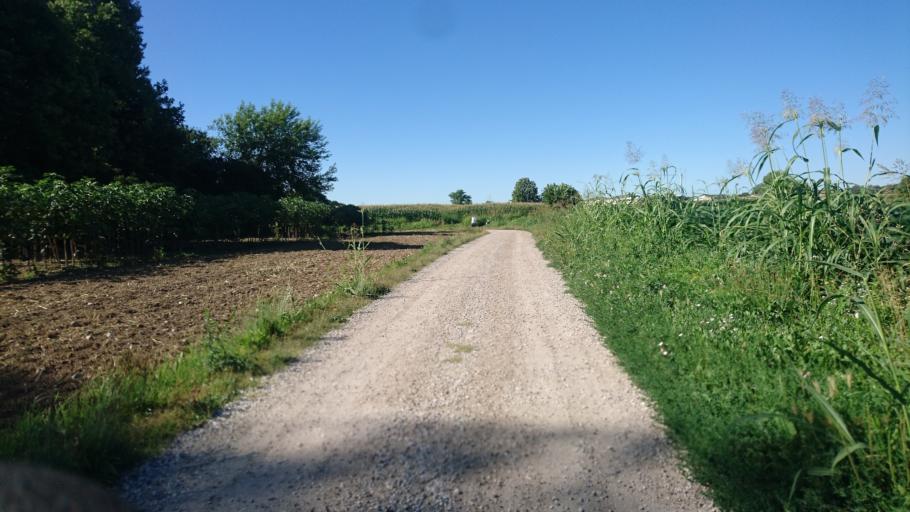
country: IT
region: Veneto
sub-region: Provincia di Padova
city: Legnaro
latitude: 45.3341
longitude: 11.9667
